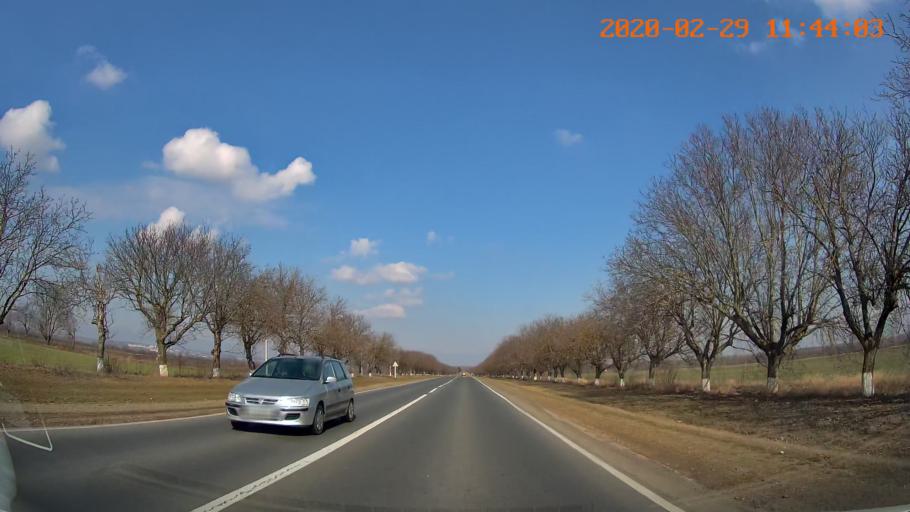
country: MD
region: Rezina
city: Saharna
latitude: 47.7055
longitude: 29.0011
